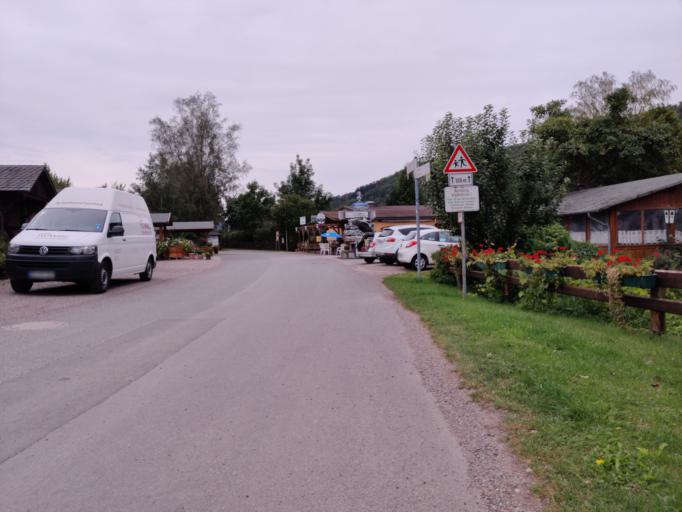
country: DE
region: Lower Saxony
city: Bodenwerder
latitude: 51.9594
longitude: 9.5054
